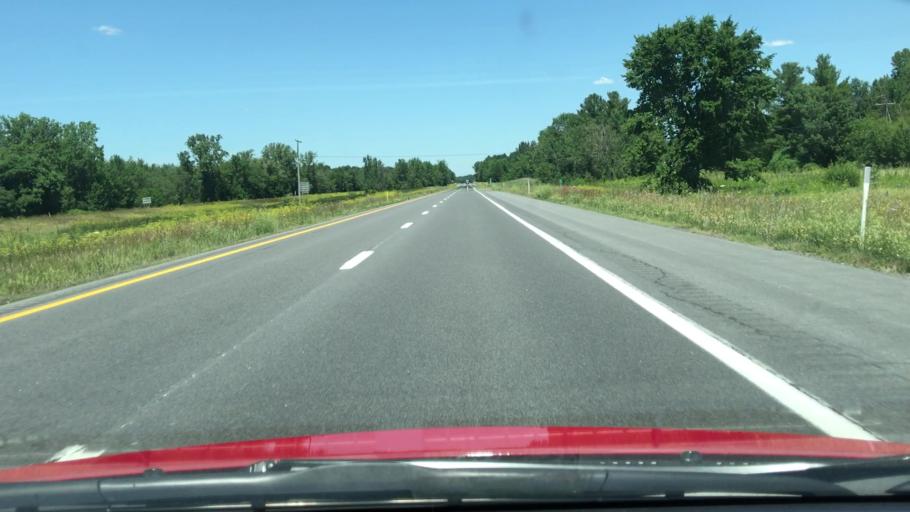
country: US
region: New York
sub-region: Clinton County
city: Cumberland Head
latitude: 44.8221
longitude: -73.4453
